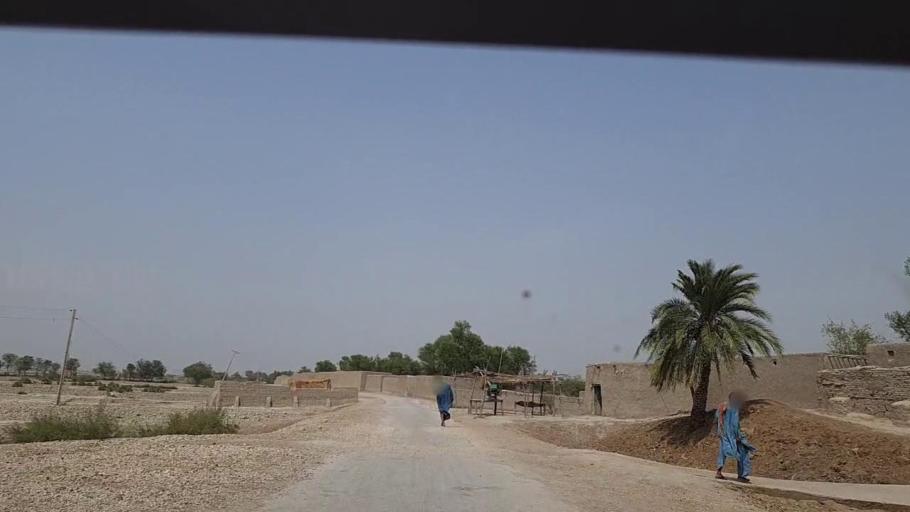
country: PK
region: Sindh
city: Khairpur Nathan Shah
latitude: 27.0487
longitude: 67.6419
